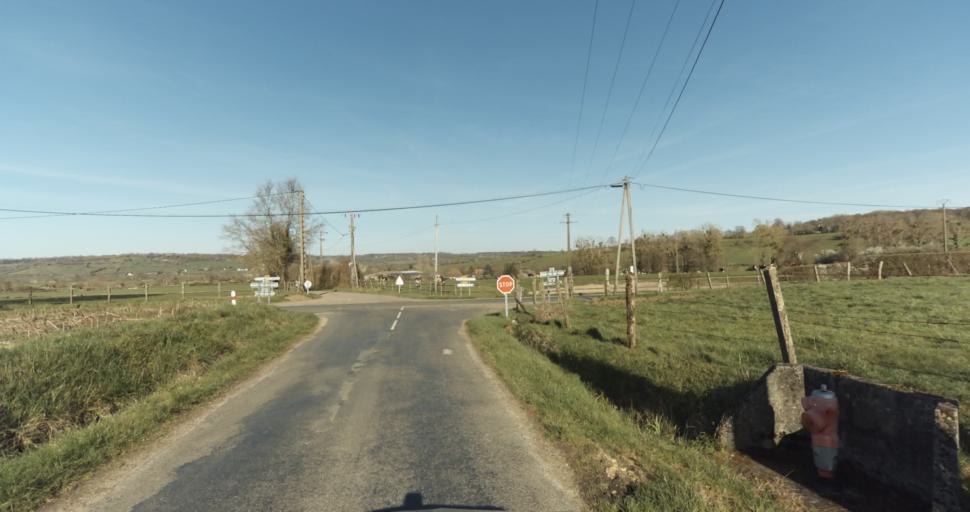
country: FR
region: Lower Normandy
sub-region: Departement du Calvados
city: Livarot
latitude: 49.0495
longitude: 0.0935
